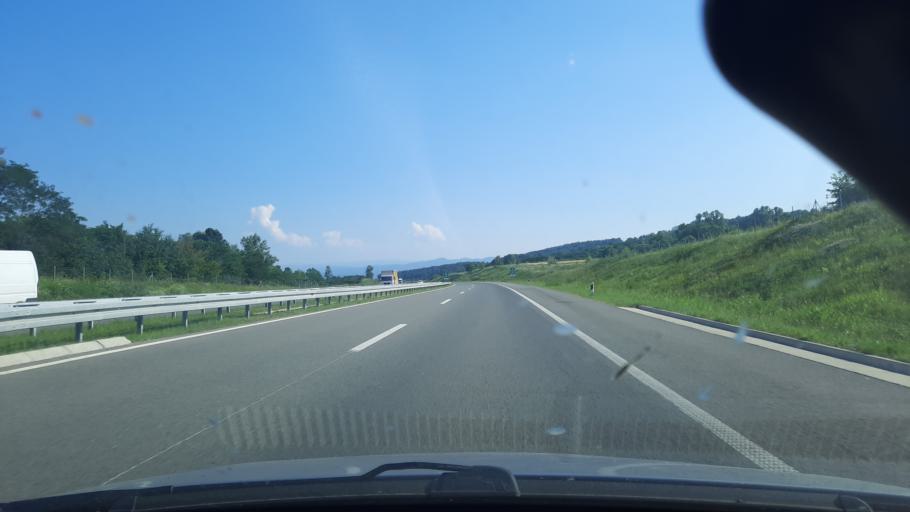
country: RS
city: Prislonica
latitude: 43.9461
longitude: 20.4000
